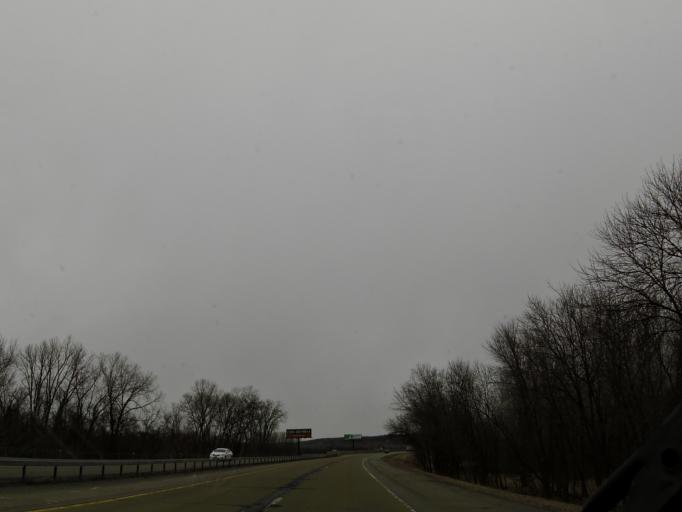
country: US
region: Minnesota
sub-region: Le Sueur County
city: Le Sueur
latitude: 44.4773
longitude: -93.9201
